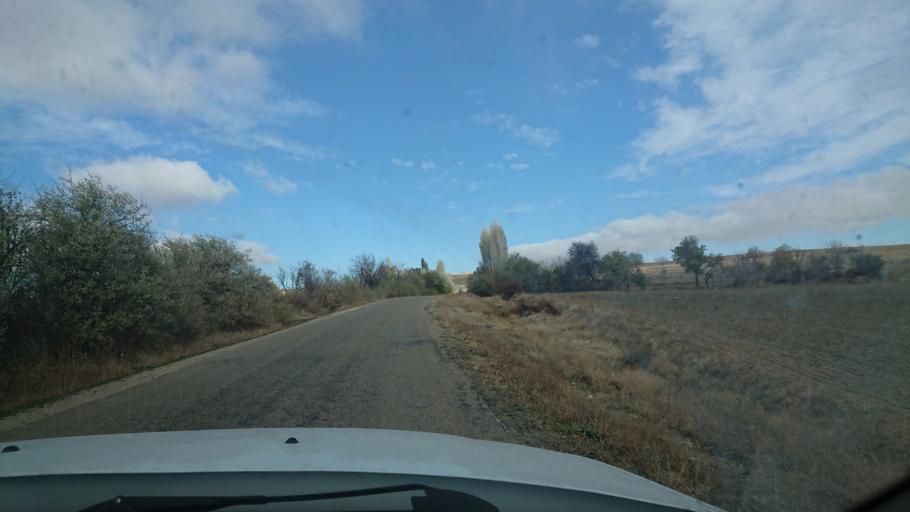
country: TR
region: Aksaray
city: Agacoren
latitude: 38.8306
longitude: 33.9560
